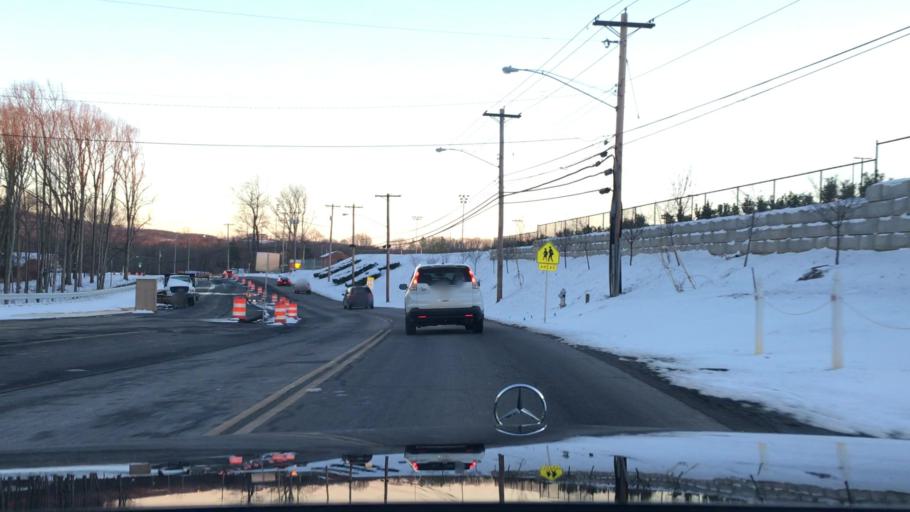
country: US
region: Virginia
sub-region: City of Lynchburg
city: West Lynchburg
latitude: 37.3643
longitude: -79.2054
